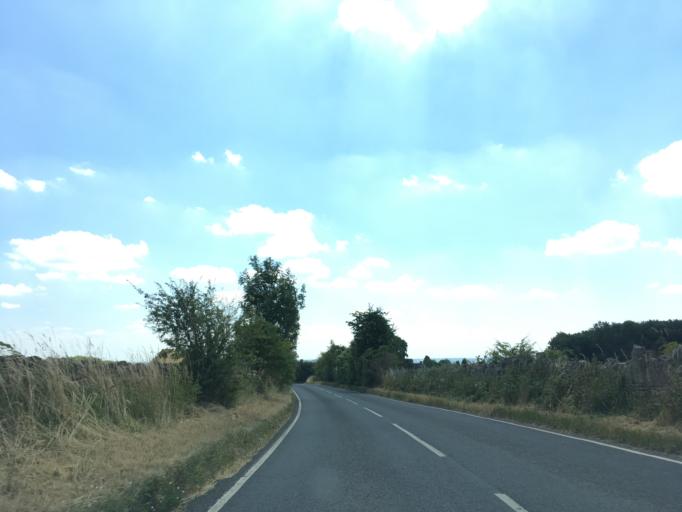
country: GB
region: England
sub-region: Gloucestershire
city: Painswick
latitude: 51.7738
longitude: -2.2361
